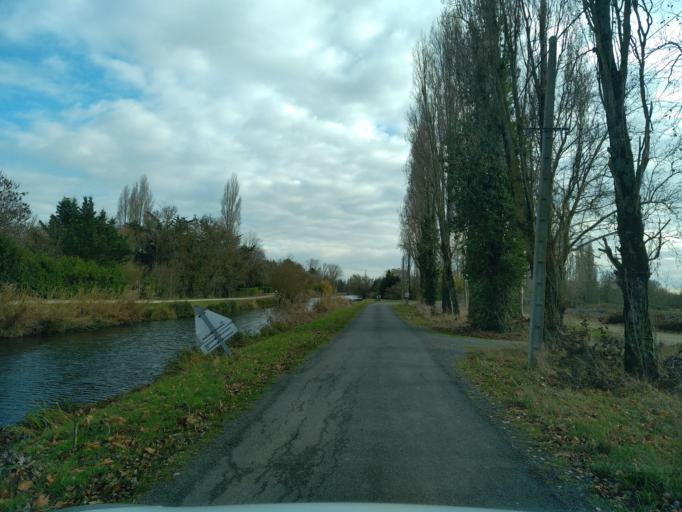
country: FR
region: Pays de la Loire
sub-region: Departement de la Vendee
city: Maillezais
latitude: 46.3149
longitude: -0.7736
